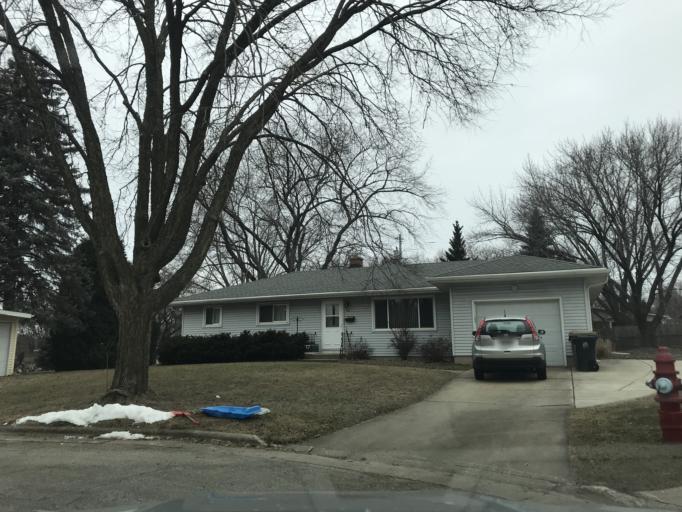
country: US
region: Wisconsin
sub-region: Dane County
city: Monona
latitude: 43.0878
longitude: -89.3014
